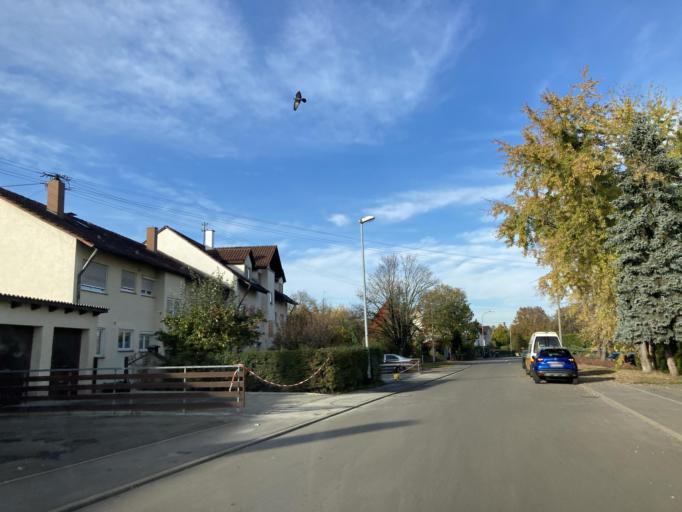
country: DE
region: Baden-Wuerttemberg
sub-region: Tuebingen Region
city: Bodelshausen
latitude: 48.3966
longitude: 8.9776
